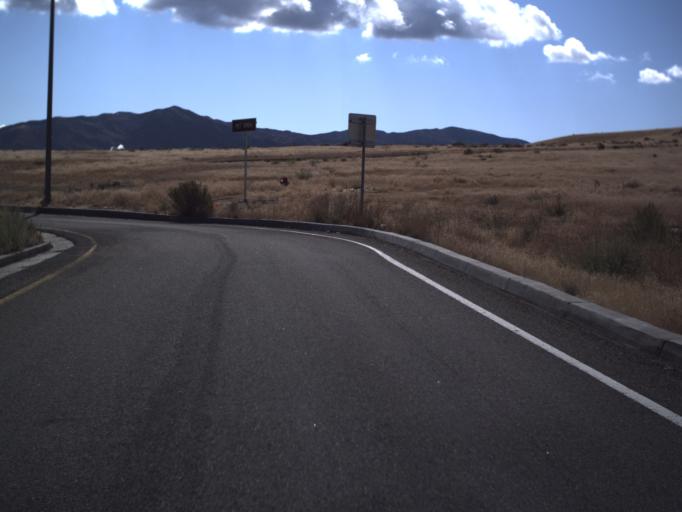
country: US
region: Utah
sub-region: Tooele County
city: Grantsville
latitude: 40.7555
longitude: -113.0191
